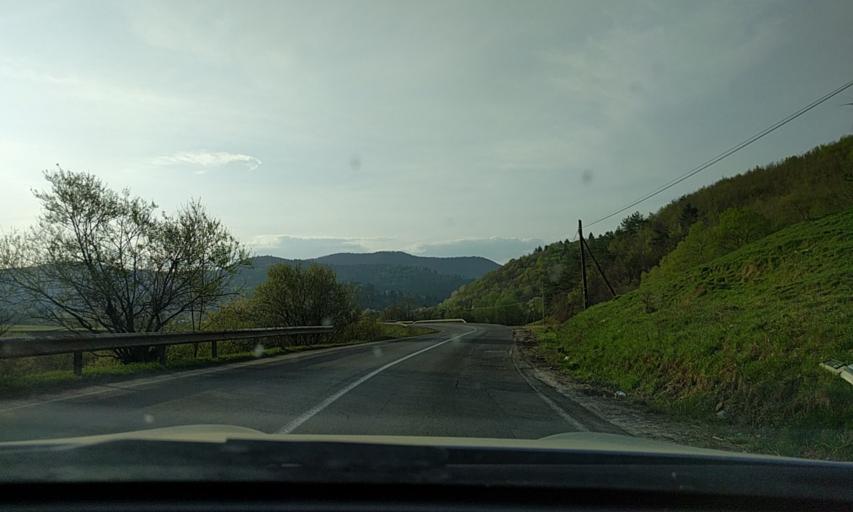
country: RO
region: Covasna
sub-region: Comuna Bretcu
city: Bretcu
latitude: 46.0473
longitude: 26.3206
